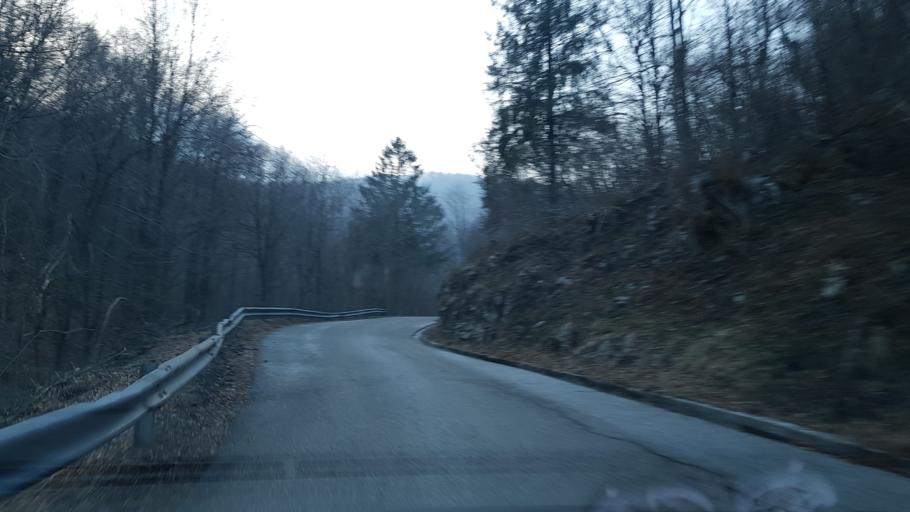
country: IT
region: Friuli Venezia Giulia
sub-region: Provincia di Udine
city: Taipana
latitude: 46.2163
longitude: 13.3911
